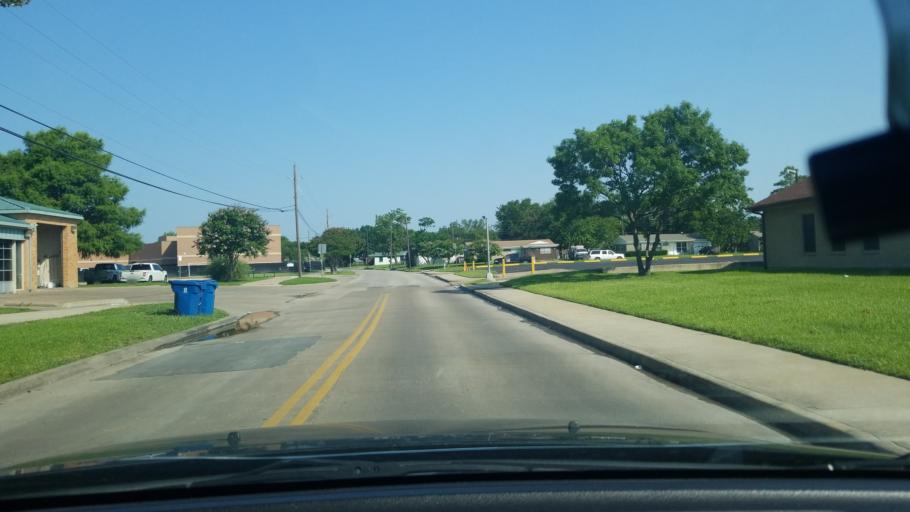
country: US
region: Texas
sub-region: Dallas County
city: Mesquite
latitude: 32.8269
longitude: -96.6428
